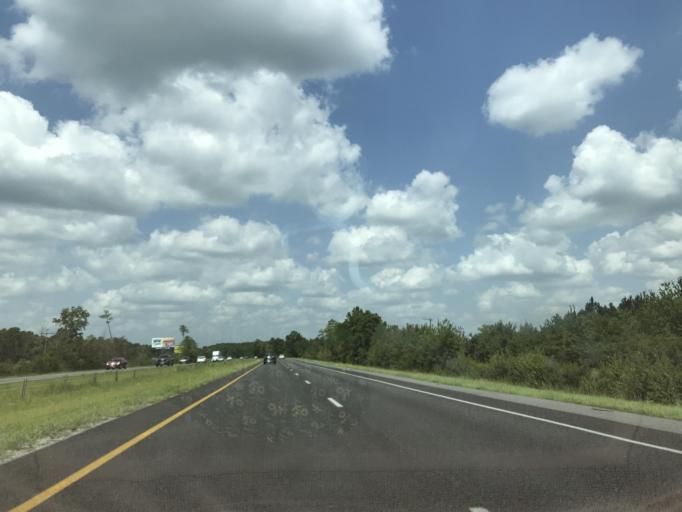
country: US
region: North Carolina
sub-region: Duplin County
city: Wallace
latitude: 34.7848
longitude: -77.9755
